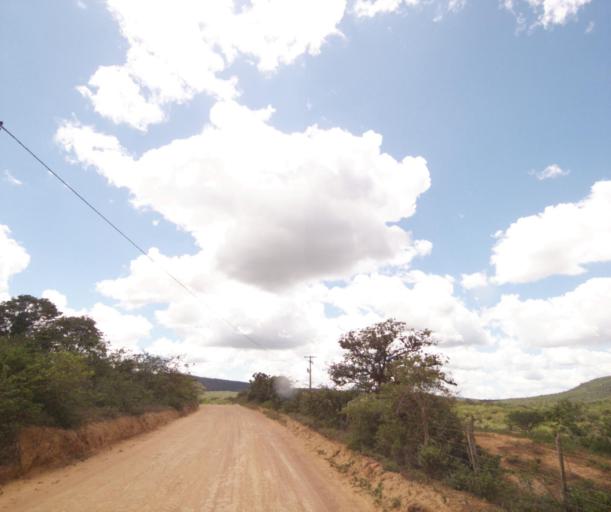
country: BR
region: Bahia
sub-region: Pocoes
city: Pocoes
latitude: -14.3896
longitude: -40.5466
